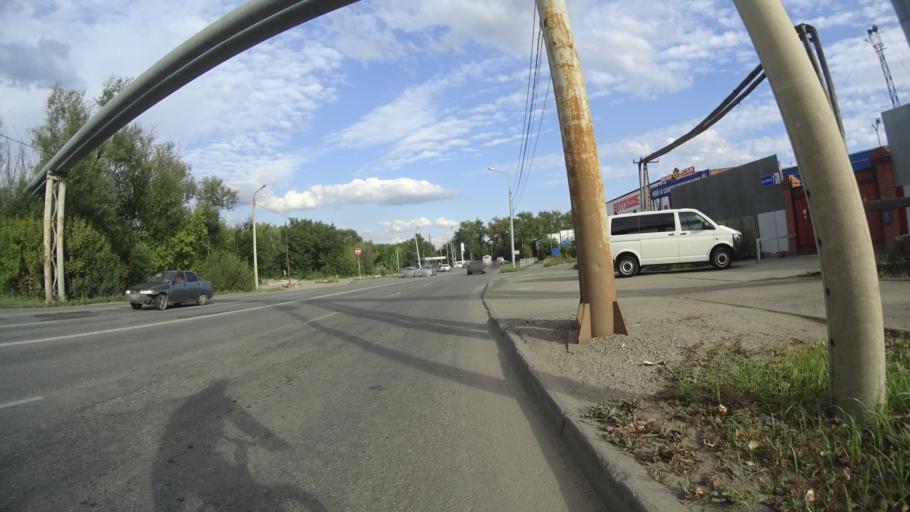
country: RU
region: Chelyabinsk
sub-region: Gorod Chelyabinsk
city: Chelyabinsk
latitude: 55.1956
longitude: 61.3819
